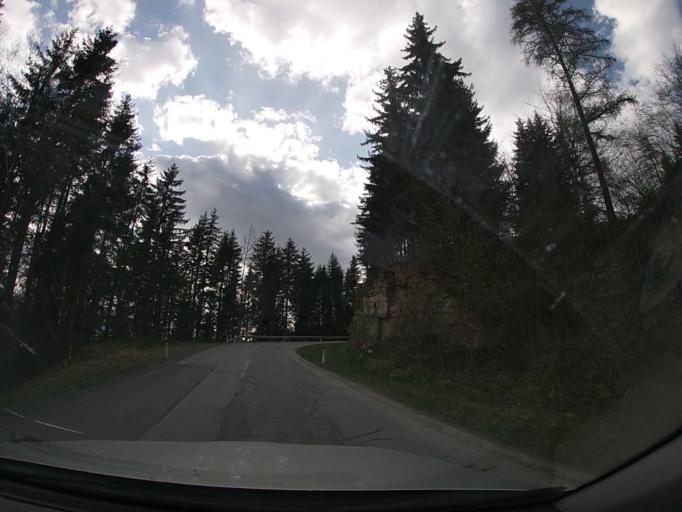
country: AT
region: Styria
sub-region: Politischer Bezirk Murau
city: Murau
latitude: 47.1188
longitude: 14.1800
